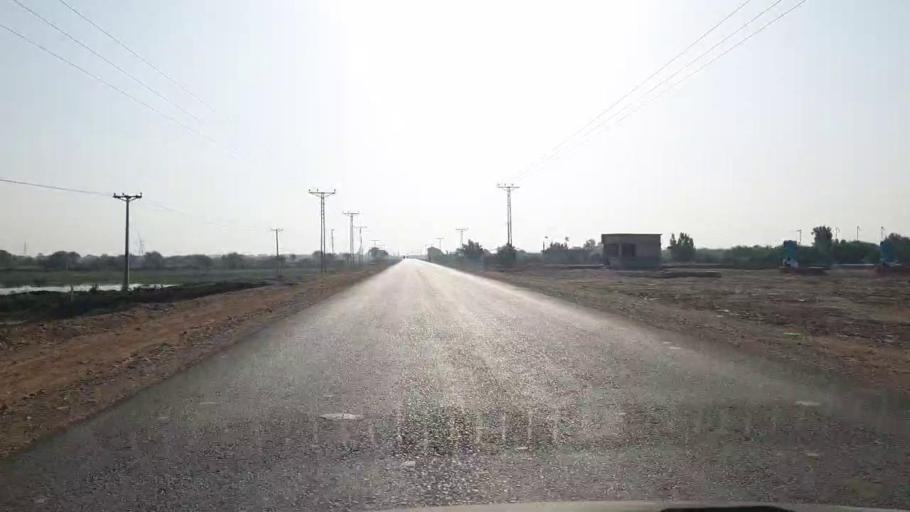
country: PK
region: Sindh
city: Badin
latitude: 24.6720
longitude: 68.8568
